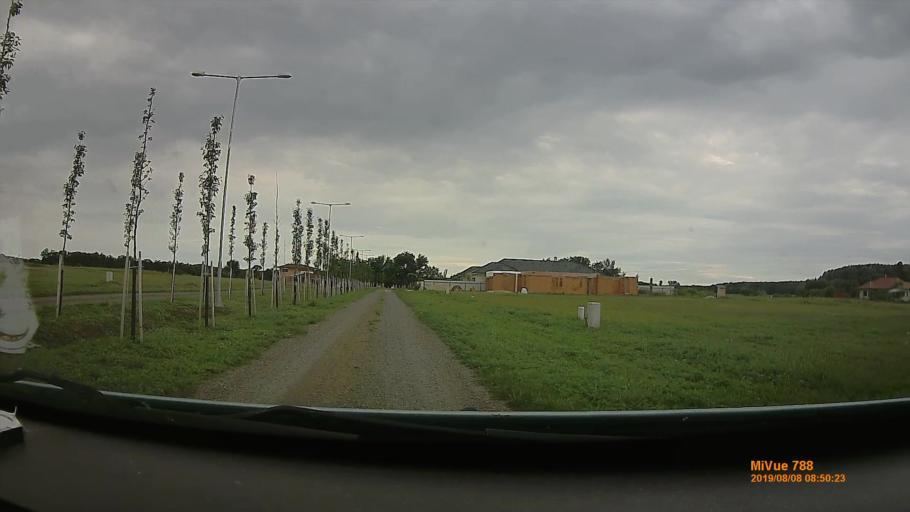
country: HU
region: Hajdu-Bihar
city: Debrecen
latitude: 47.6006
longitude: 21.6440
